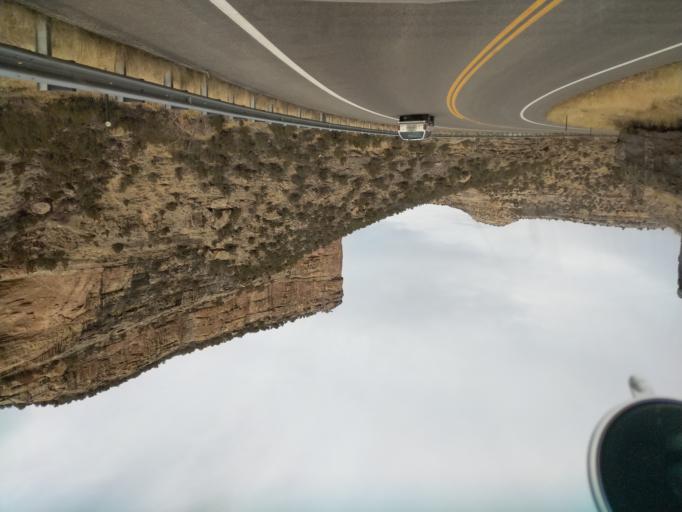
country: US
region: Colorado
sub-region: Mesa County
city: Palisade
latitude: 39.1884
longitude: -108.2445
